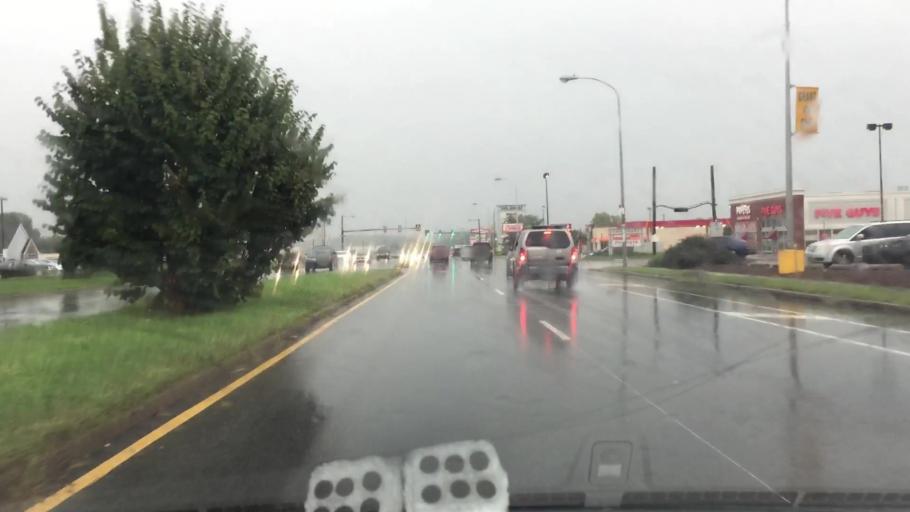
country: US
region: Pennsylvania
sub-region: Montgomery County
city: Rockledge
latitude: 40.0794
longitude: -75.0280
